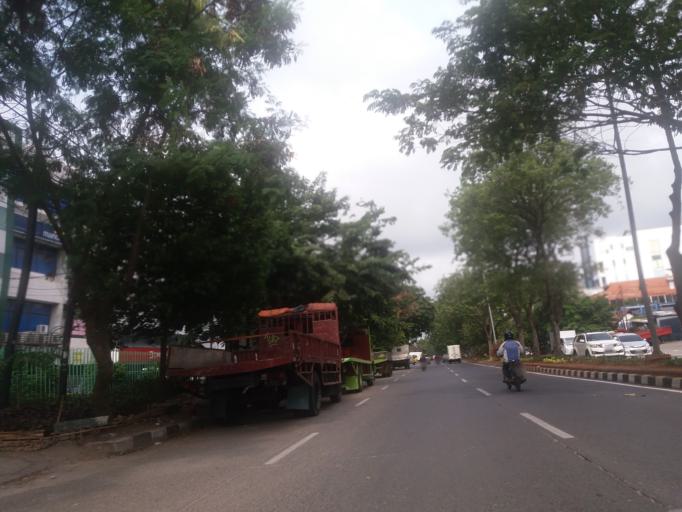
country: ID
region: Jakarta Raya
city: Jakarta
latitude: -6.1416
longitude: 106.8278
